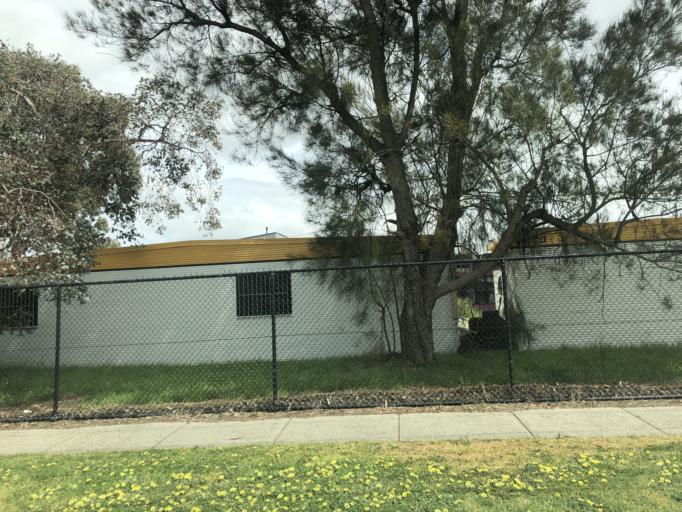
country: AU
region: Victoria
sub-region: Greater Dandenong
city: Dandenong North
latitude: -37.9570
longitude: 145.2073
